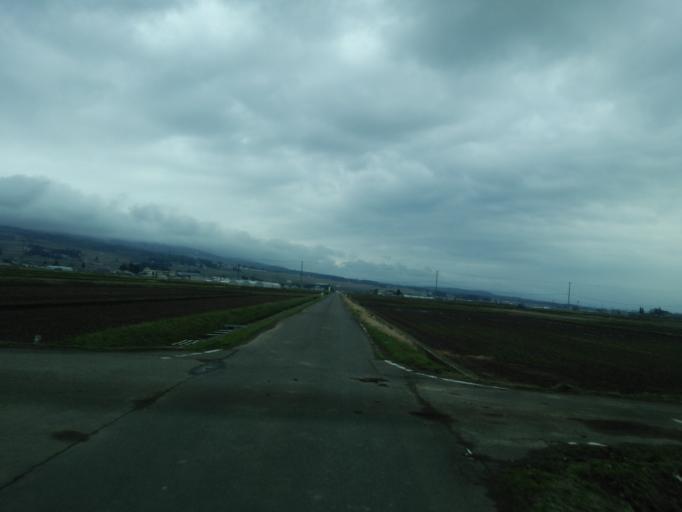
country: JP
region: Fukushima
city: Kitakata
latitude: 37.6499
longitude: 139.9152
